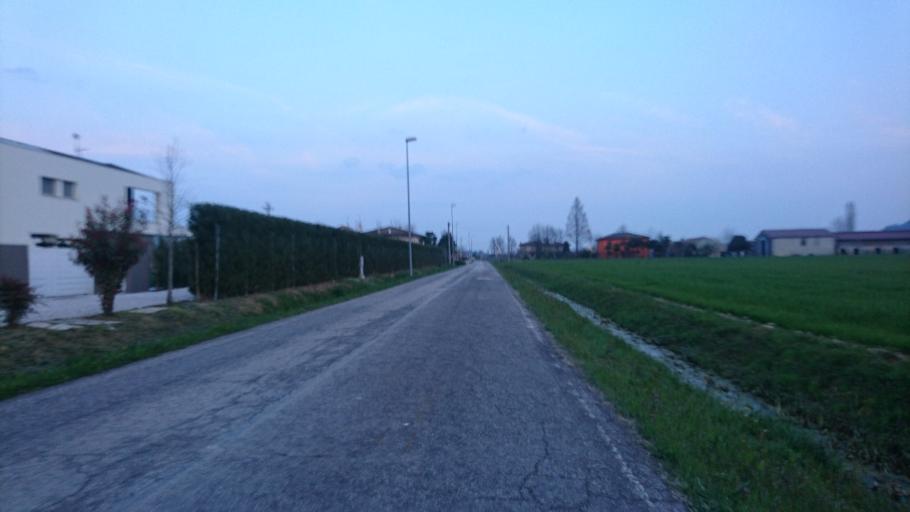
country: IT
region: Veneto
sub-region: Provincia di Padova
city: Saccolongo
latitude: 45.3954
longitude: 11.7341
